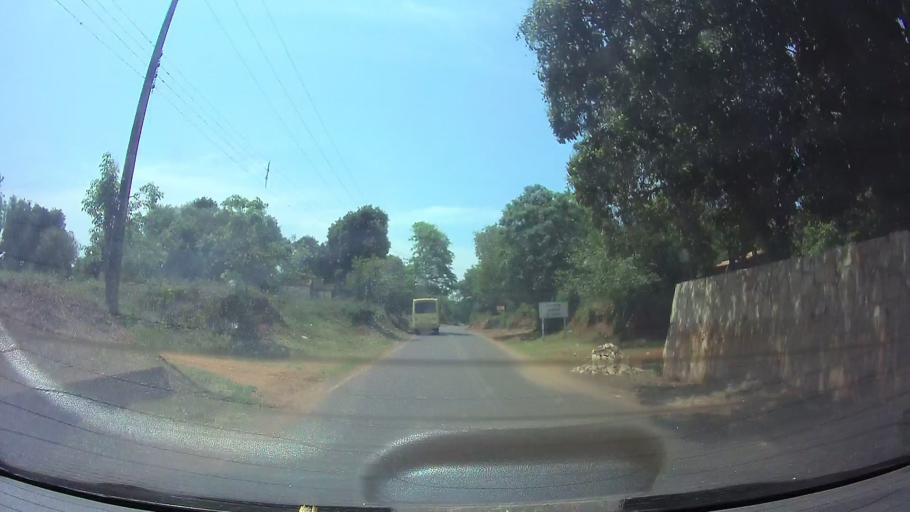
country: PY
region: Central
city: Ita
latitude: -25.4405
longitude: -57.4008
